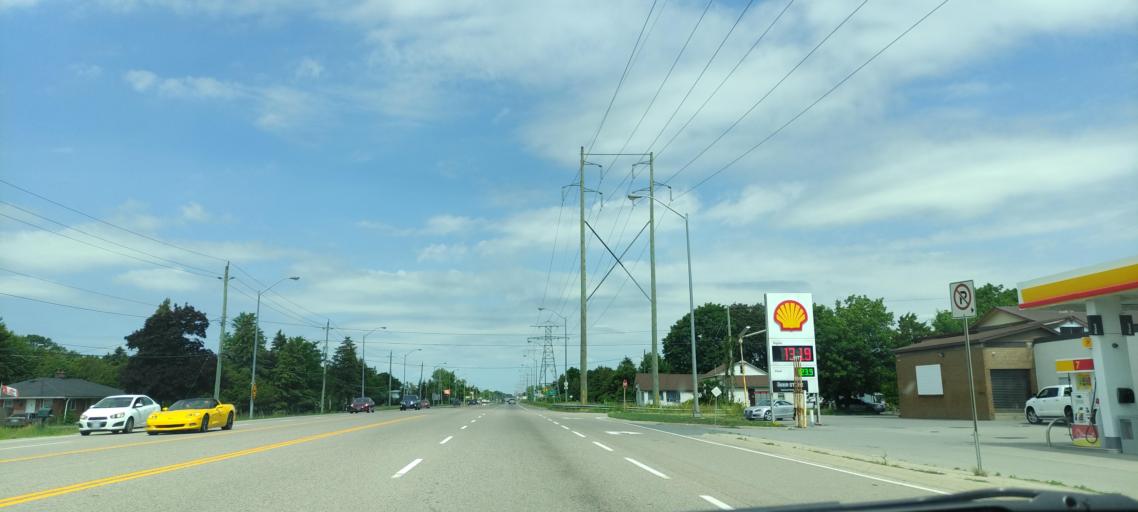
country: CA
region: Ontario
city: Ancaster
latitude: 43.3647
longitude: -79.9894
